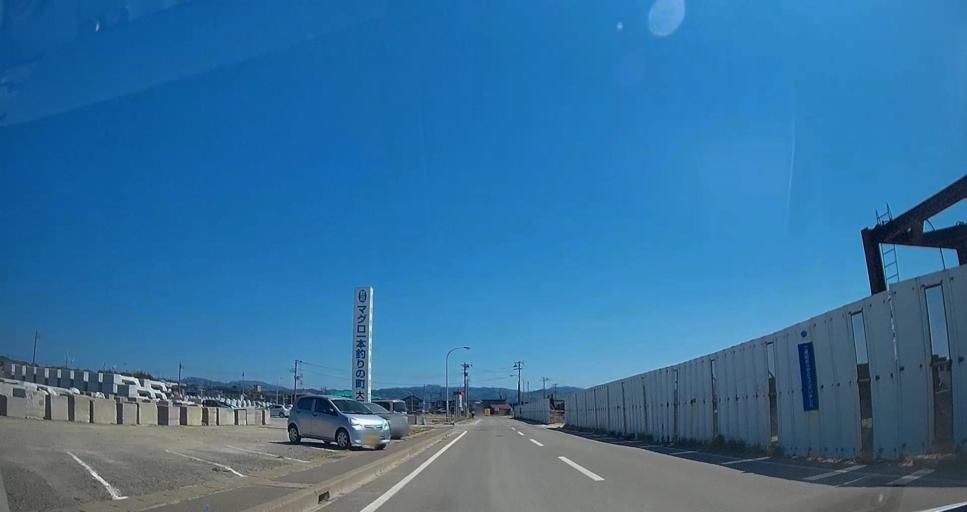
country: JP
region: Hokkaido
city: Hakodate
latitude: 41.5247
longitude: 140.8997
